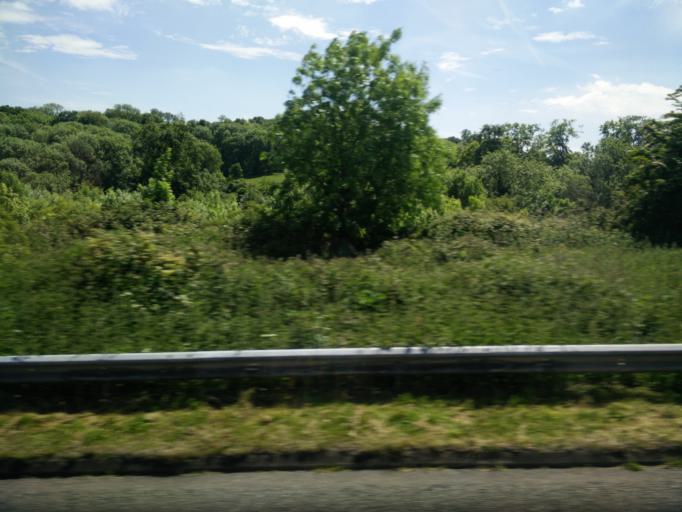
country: GB
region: England
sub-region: Hertfordshire
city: Hitchin
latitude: 51.9344
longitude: -0.3365
